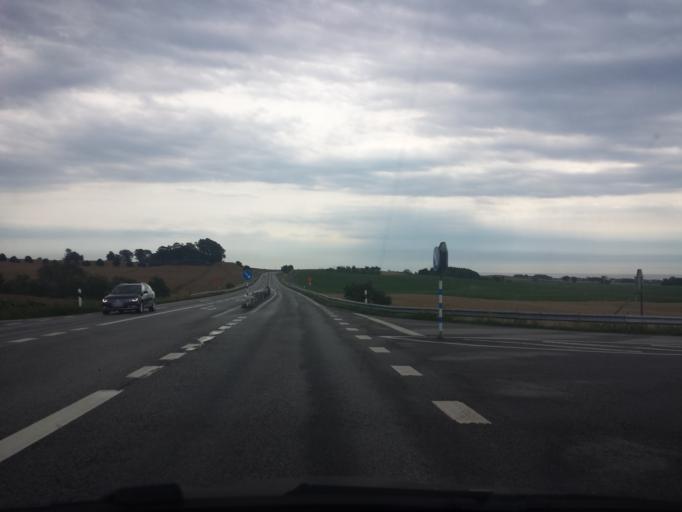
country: SE
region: Skane
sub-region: Ystads Kommun
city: Ystad
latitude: 55.4499
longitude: 13.7640
